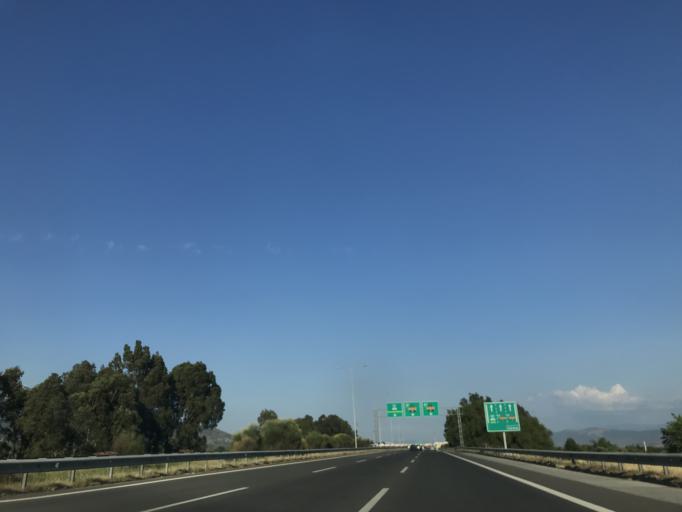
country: TR
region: Aydin
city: Acarlar
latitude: 37.8616
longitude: 27.7815
